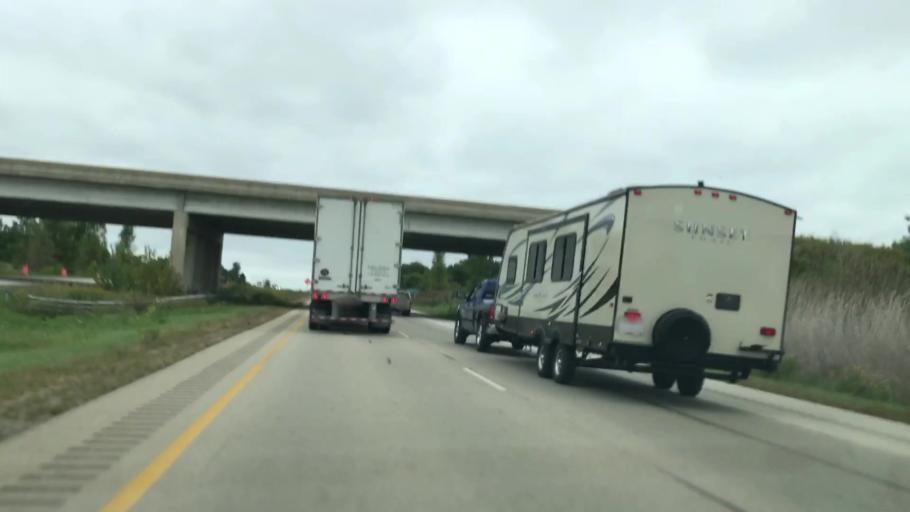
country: US
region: Wisconsin
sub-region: Brown County
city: Suamico
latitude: 44.6779
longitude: -88.0505
